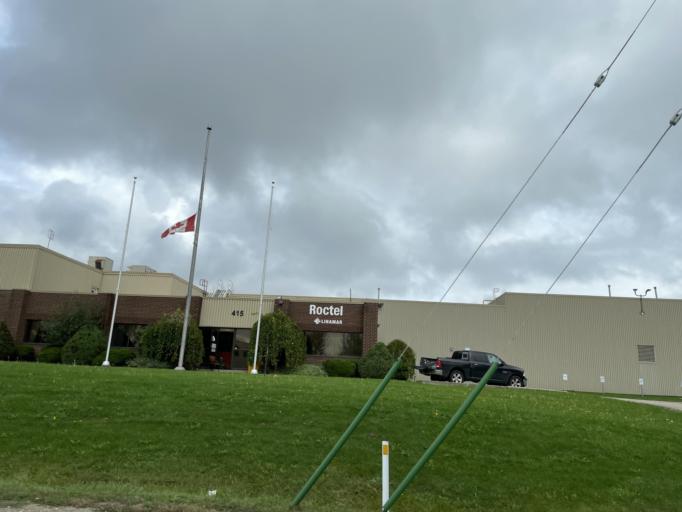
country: CA
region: Ontario
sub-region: Wellington County
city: Guelph
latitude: 43.5346
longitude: -80.3090
